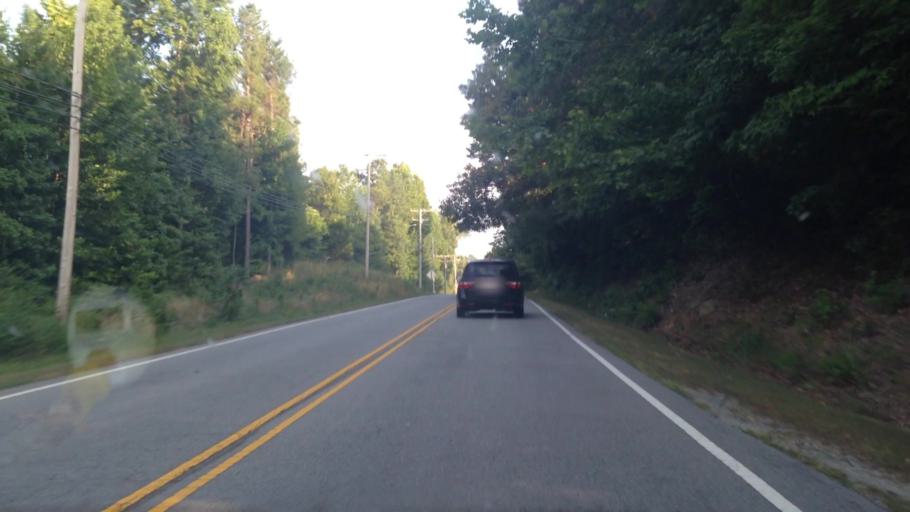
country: US
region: North Carolina
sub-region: Davidson County
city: Thomasville
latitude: 35.9459
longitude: -80.0756
